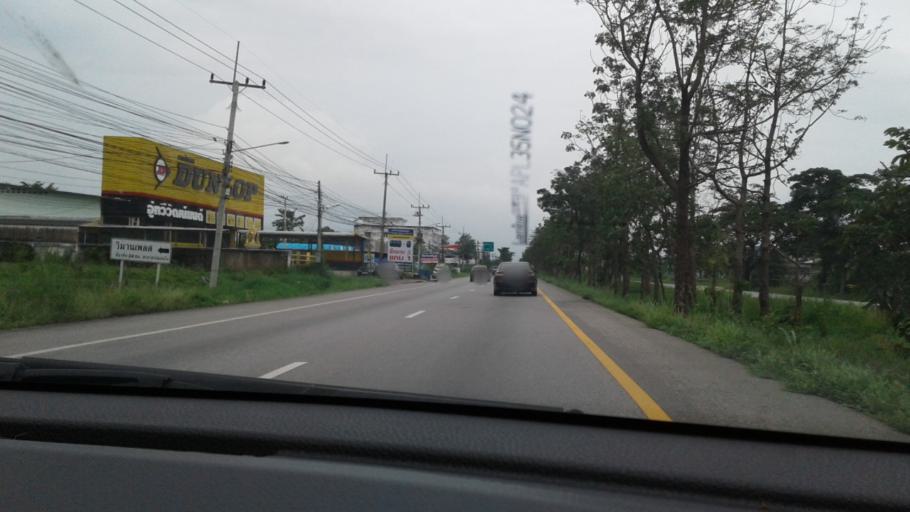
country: TH
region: Prachuap Khiri Khan
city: Prachuap Khiri Khan
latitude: 11.7990
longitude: 99.7759
